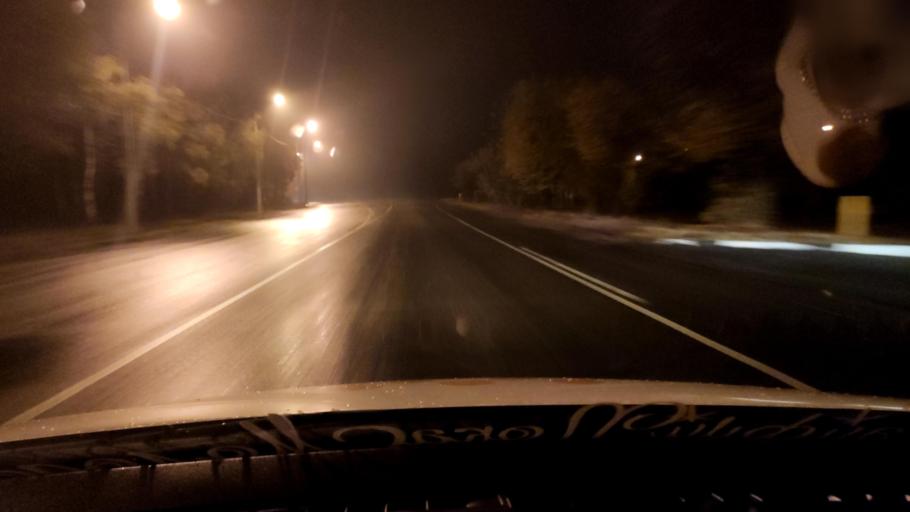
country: RU
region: Voronezj
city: Pridonskoy
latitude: 51.7010
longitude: 39.0783
